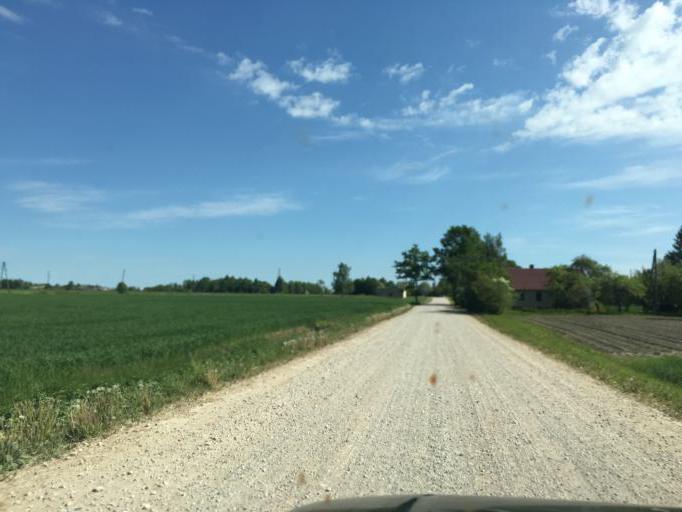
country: LV
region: Talsu Rajons
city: Valdemarpils
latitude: 57.3393
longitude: 22.4838
